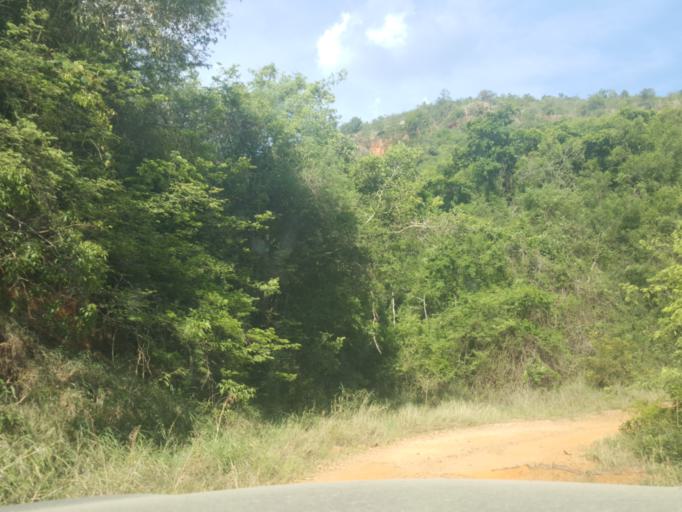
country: ZA
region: Limpopo
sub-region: Mopani District Municipality
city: Hoedspruit
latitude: -24.5902
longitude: 30.8304
